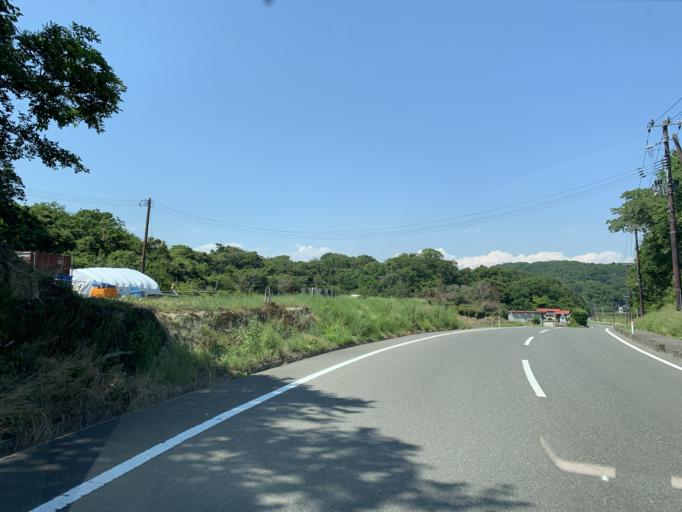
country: JP
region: Miyagi
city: Matsushima
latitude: 38.3268
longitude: 141.1550
